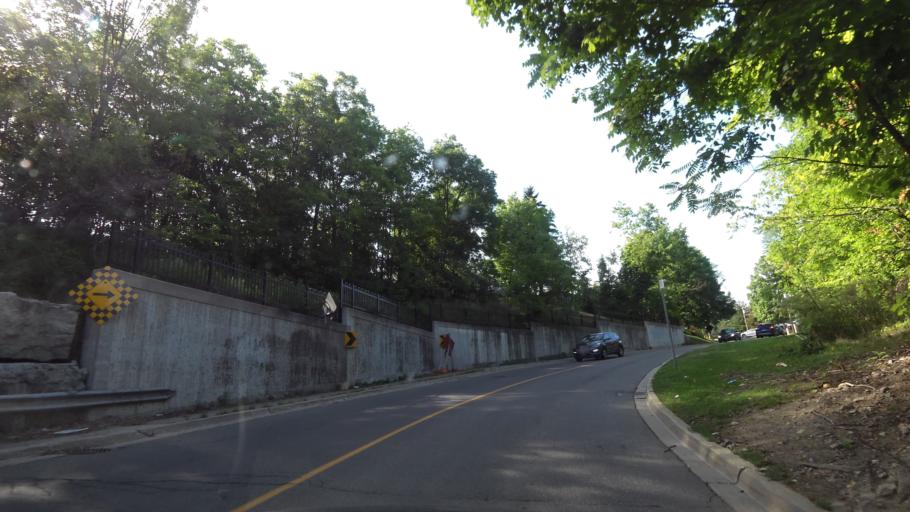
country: CA
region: Ontario
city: Burlington
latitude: 43.3314
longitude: -79.8887
